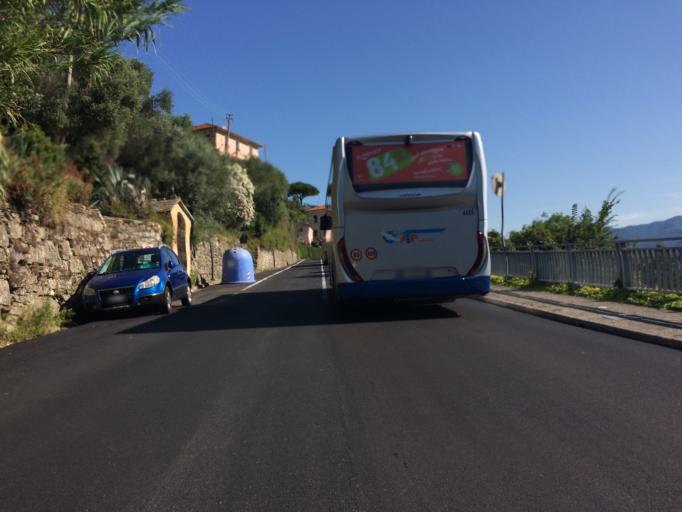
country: IT
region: Liguria
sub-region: Provincia di Genova
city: Camogli
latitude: 44.3404
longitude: 9.1819
